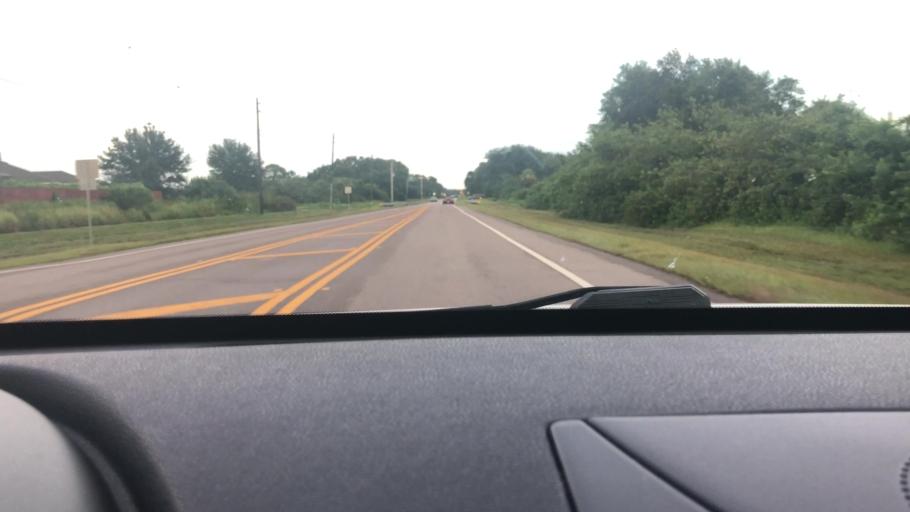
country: US
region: Florida
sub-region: Charlotte County
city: Port Charlotte
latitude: 27.0690
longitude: -82.1175
